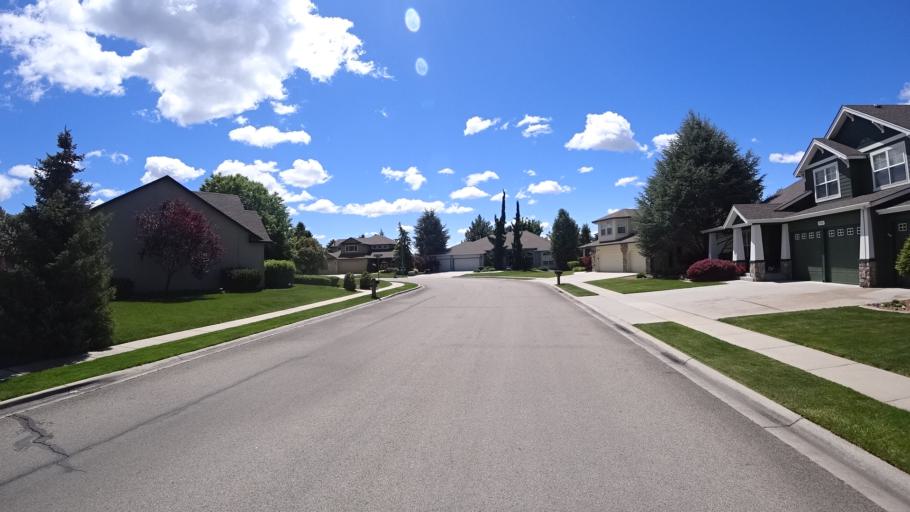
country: US
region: Idaho
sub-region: Ada County
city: Eagle
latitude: 43.6529
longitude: -116.3527
